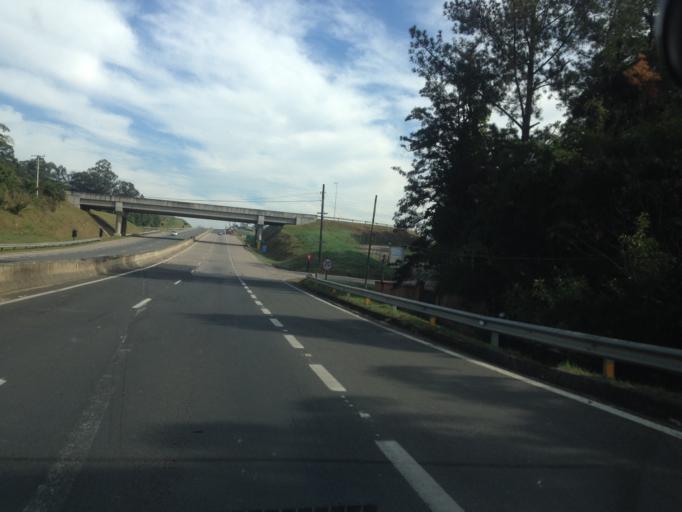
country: BR
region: Sao Paulo
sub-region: Itu
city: Itu
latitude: -23.2425
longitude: -47.3726
